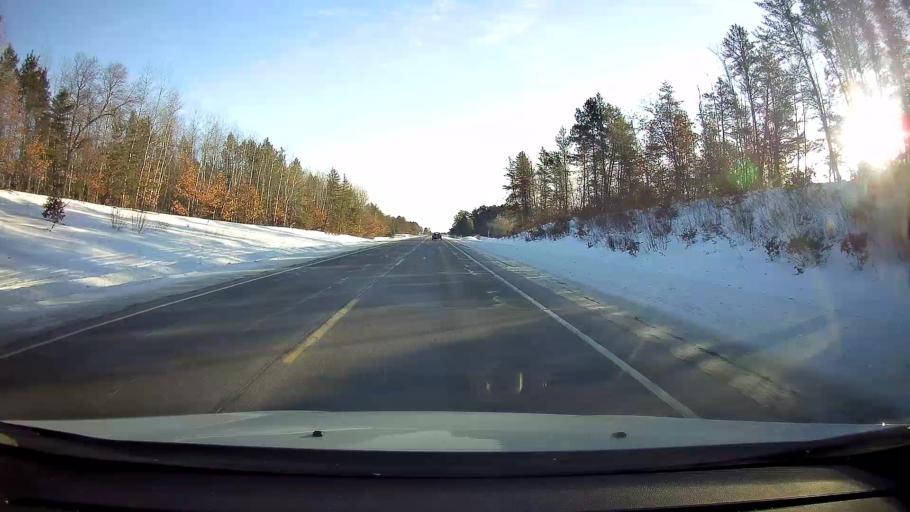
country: US
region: Wisconsin
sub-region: Washburn County
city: Spooner
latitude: 45.9104
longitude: -91.7791
